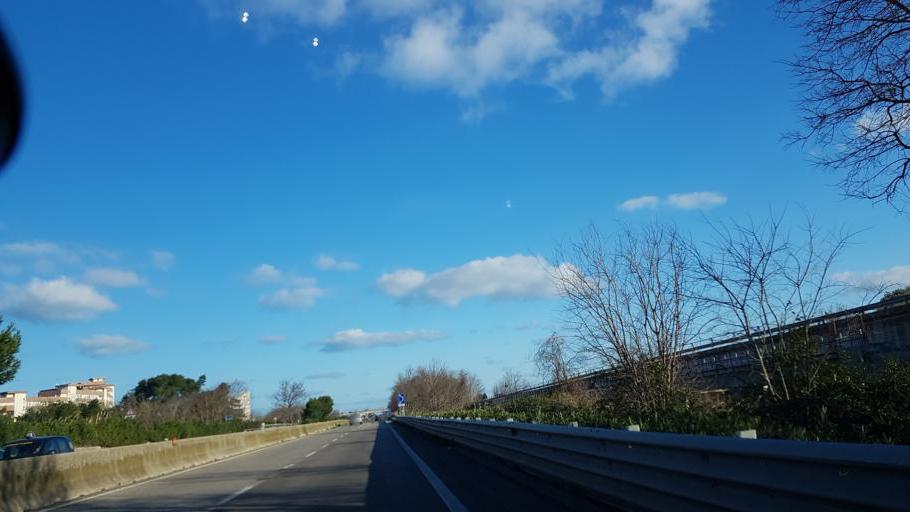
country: IT
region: Apulia
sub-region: Provincia di Brindisi
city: Brindisi
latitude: 40.6198
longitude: 17.9358
